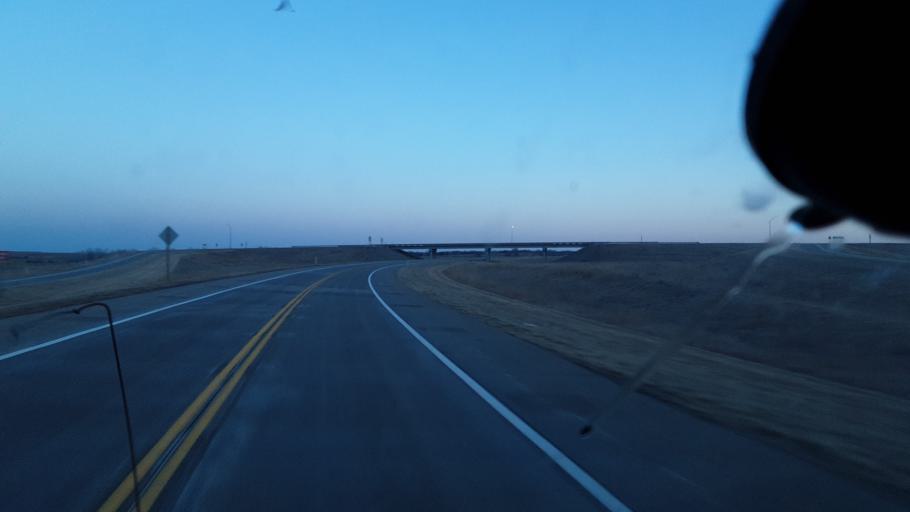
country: US
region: Kansas
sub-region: Reno County
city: South Hutchinson
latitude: 38.0324
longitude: -97.9849
